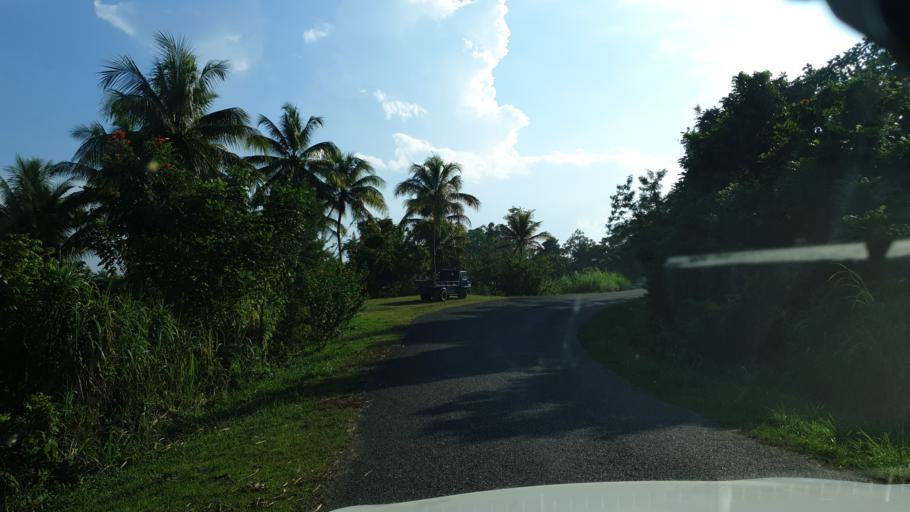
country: PG
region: East Sepik
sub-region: Wewak
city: Wewak
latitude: -3.6998
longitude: 143.6448
